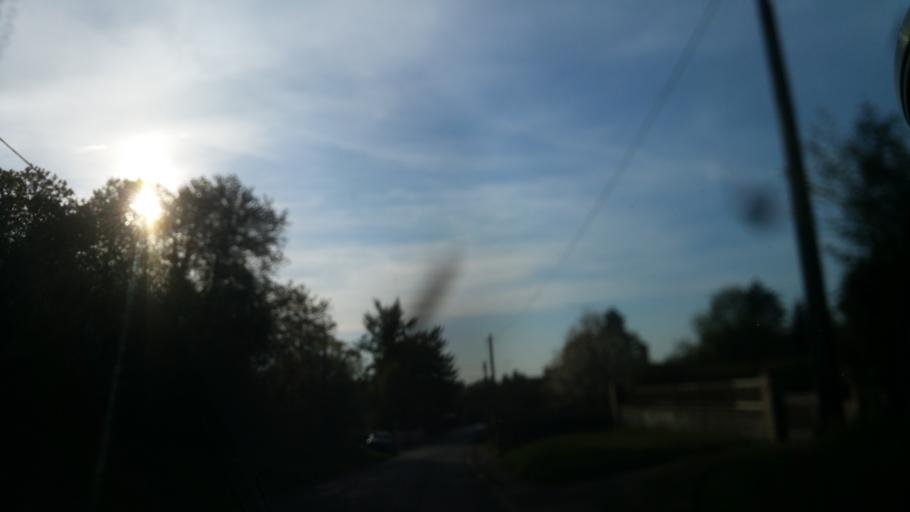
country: FR
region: Ile-de-France
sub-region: Departement de l'Essonne
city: Saint-Cyr-sous-Dourdan
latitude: 48.5645
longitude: 2.0413
